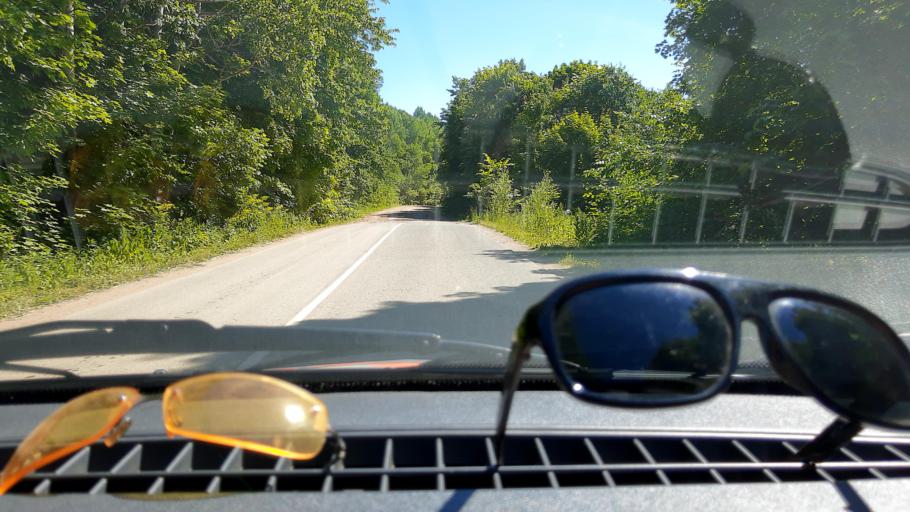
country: RU
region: Bashkortostan
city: Ulu-Telyak
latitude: 54.8071
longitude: 57.0363
